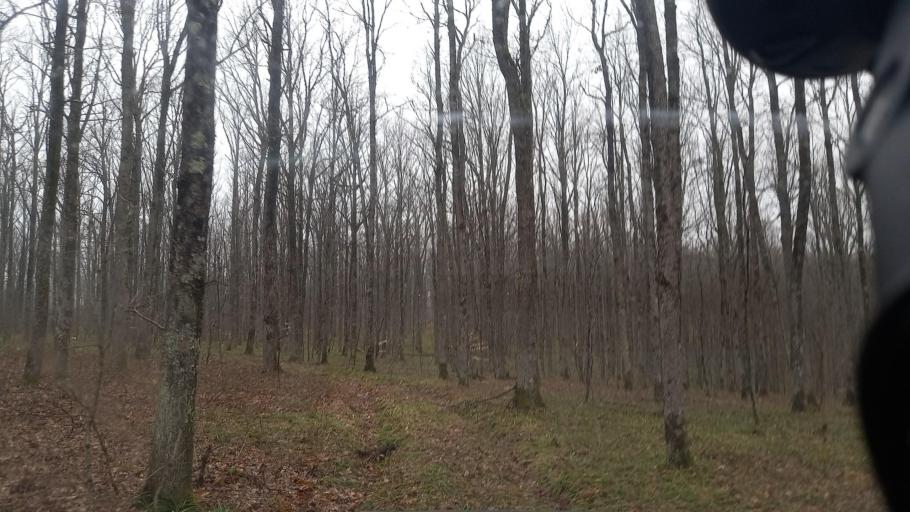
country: RU
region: Krasnodarskiy
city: Saratovskaya
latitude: 44.6541
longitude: 39.2413
